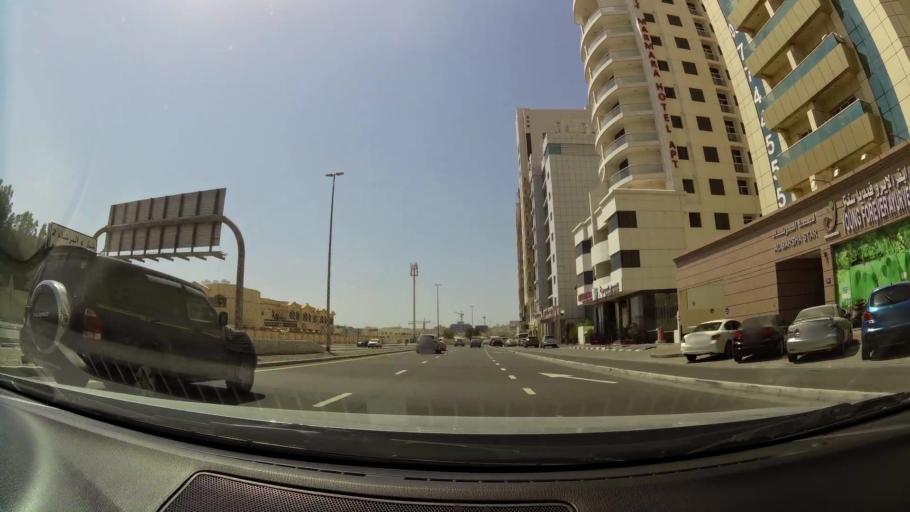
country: AE
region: Dubai
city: Dubai
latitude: 25.1090
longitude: 55.2032
